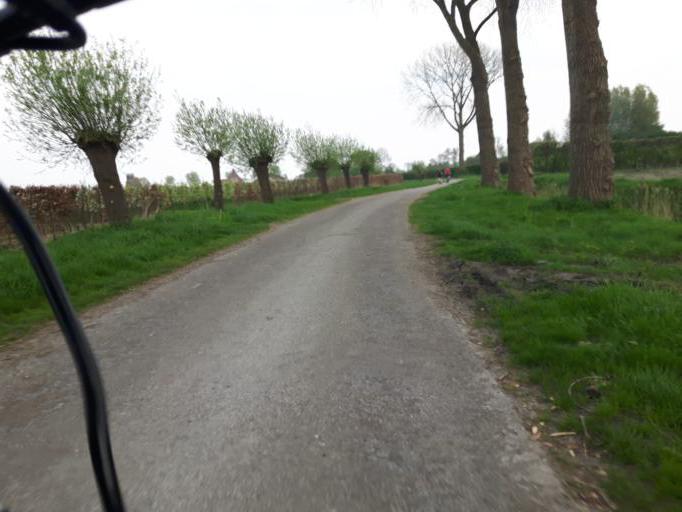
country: NL
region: Zeeland
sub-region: Gemeente Goes
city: Goes
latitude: 51.4595
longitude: 3.8414
